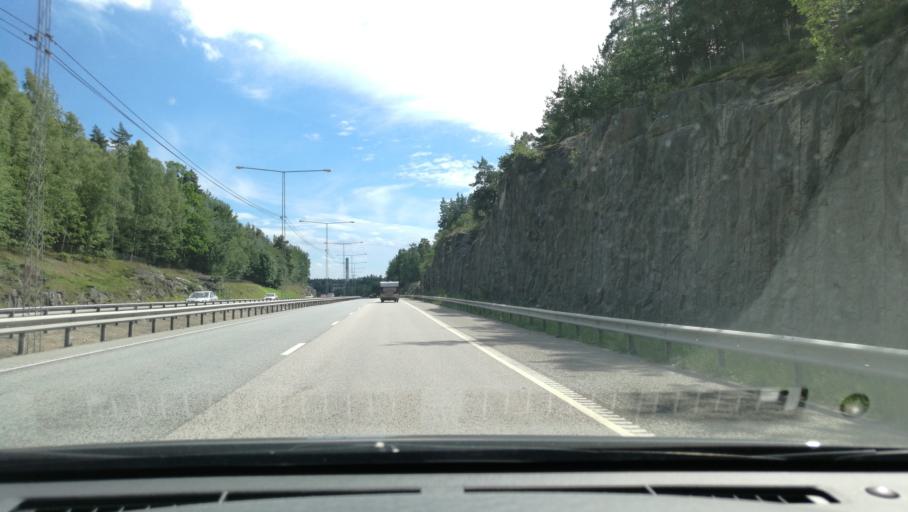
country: SE
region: Stockholm
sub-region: Jarfalla Kommun
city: Jakobsberg
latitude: 59.4387
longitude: 17.8432
